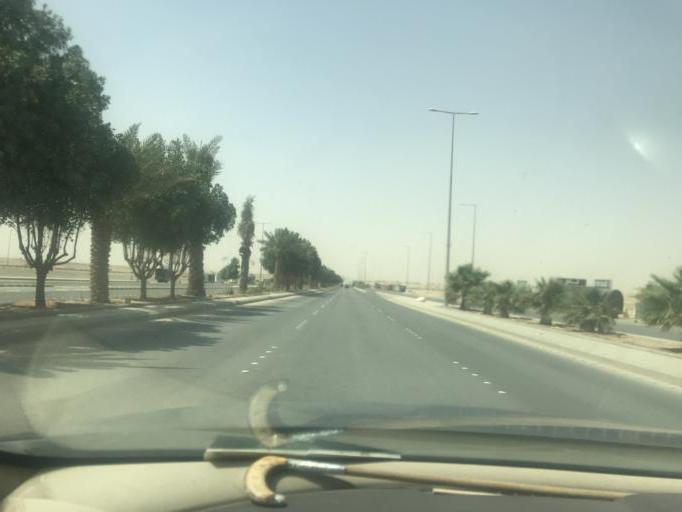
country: SA
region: Ar Riyad
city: Riyadh
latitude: 24.8035
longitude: 46.5823
